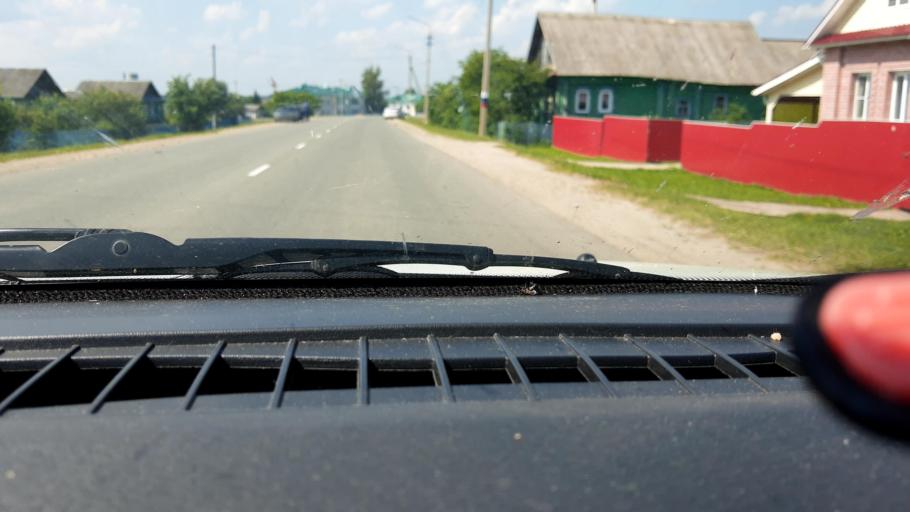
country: RU
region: Nizjnij Novgorod
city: Sharanga
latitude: 57.1842
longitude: 46.5349
